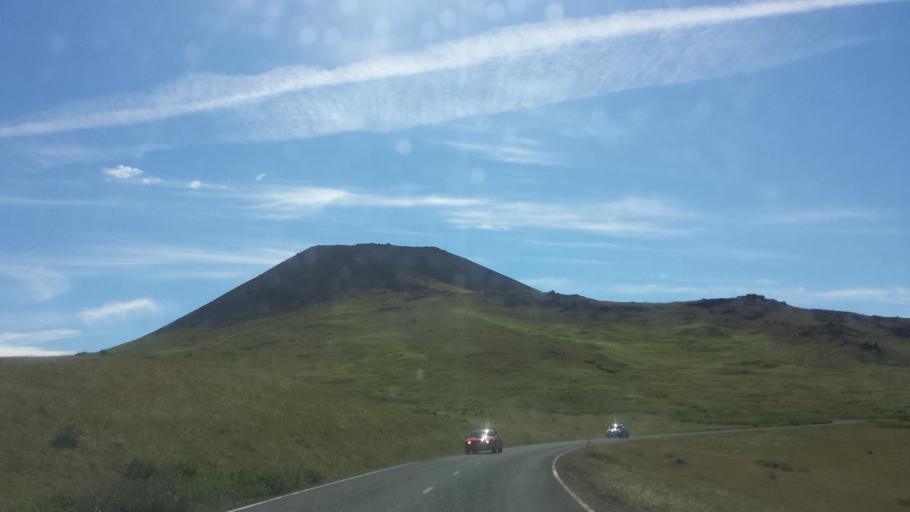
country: IS
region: South
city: Vestmannaeyjar
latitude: 63.4347
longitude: -20.2585
